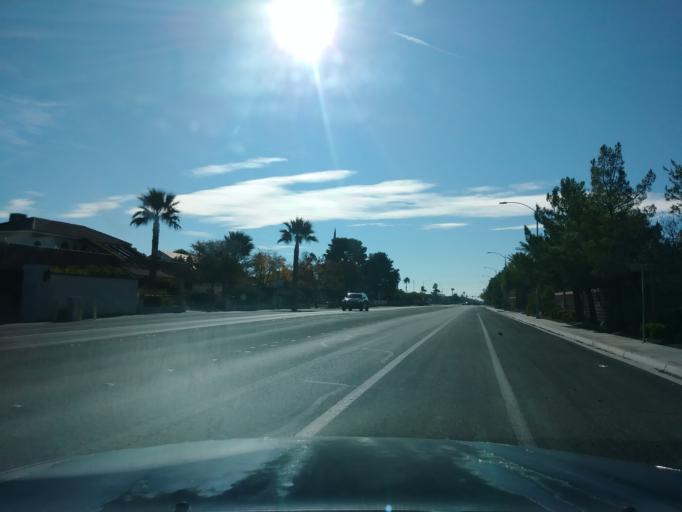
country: US
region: Nevada
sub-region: Clark County
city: Spring Valley
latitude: 36.1475
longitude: -115.2703
